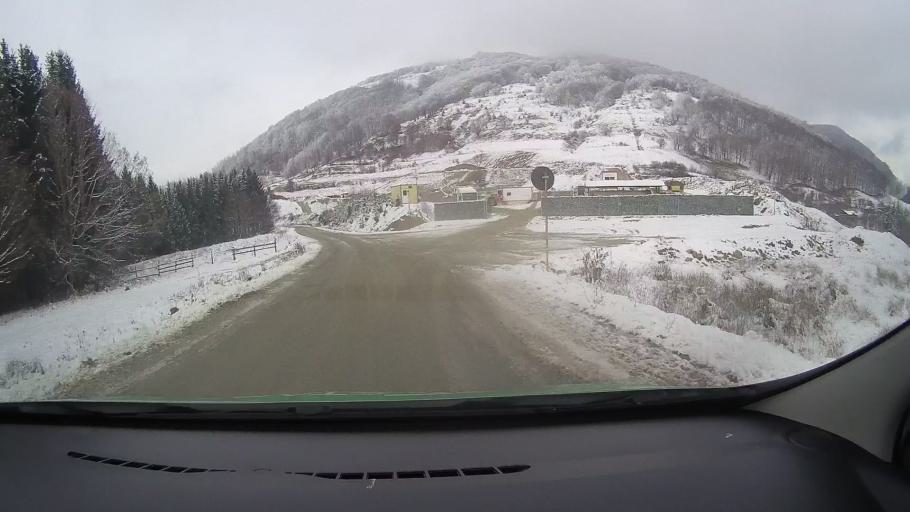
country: RO
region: Alba
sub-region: Comuna Almasu Mare
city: Almasu Mare
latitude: 46.0981
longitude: 23.1587
